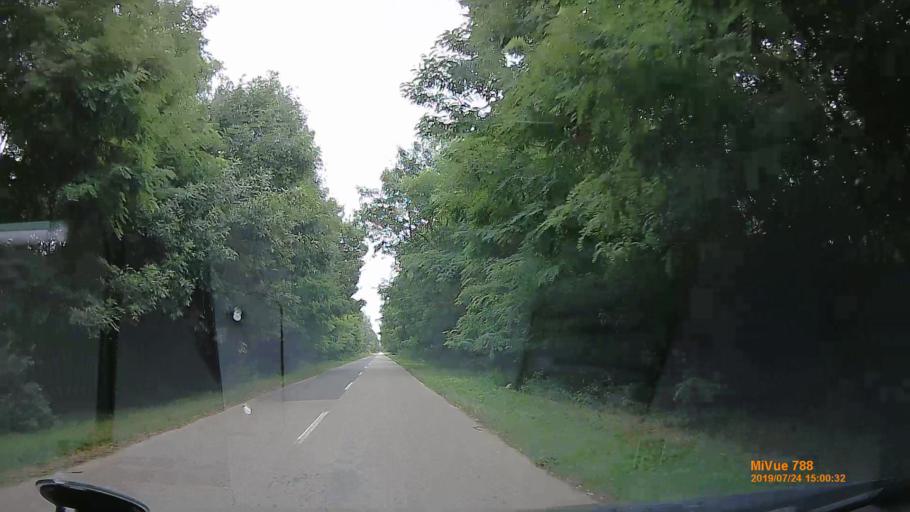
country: HU
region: Szabolcs-Szatmar-Bereg
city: Aranyosapati
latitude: 48.2321
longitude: 22.3716
